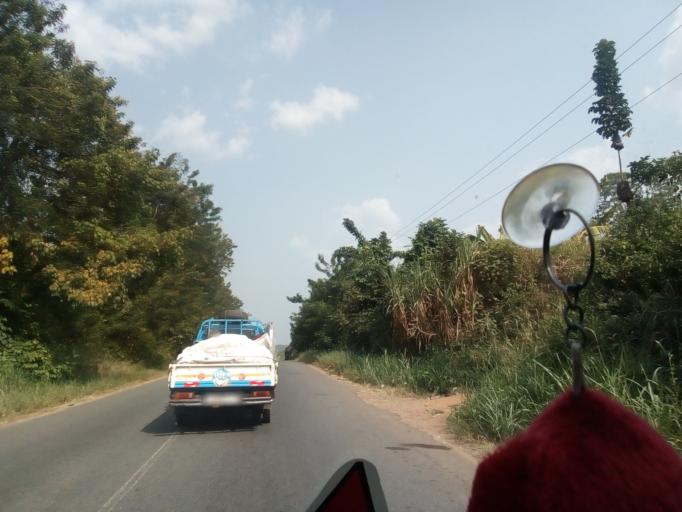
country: GH
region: Eastern
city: Suhum
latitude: 6.0435
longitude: -0.4282
